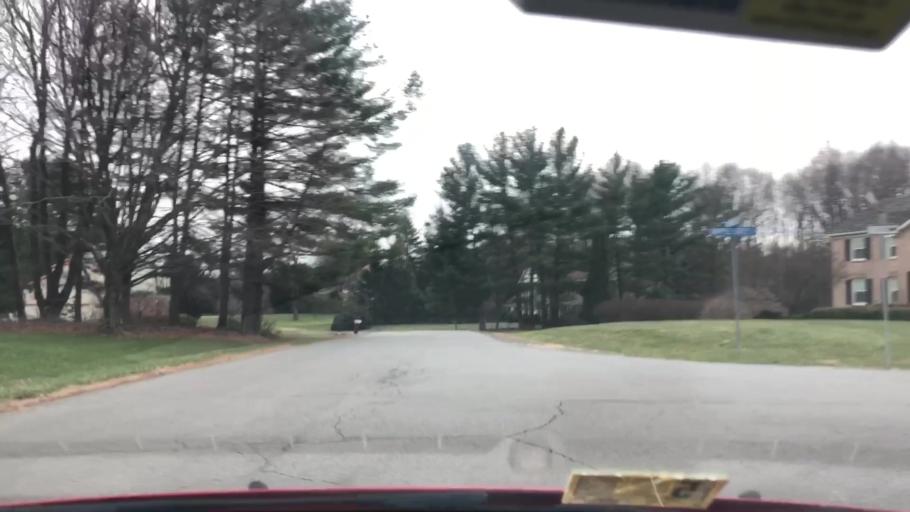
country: US
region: Virginia
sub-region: Fairfax County
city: Wolf Trap
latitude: 38.9681
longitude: -77.2745
